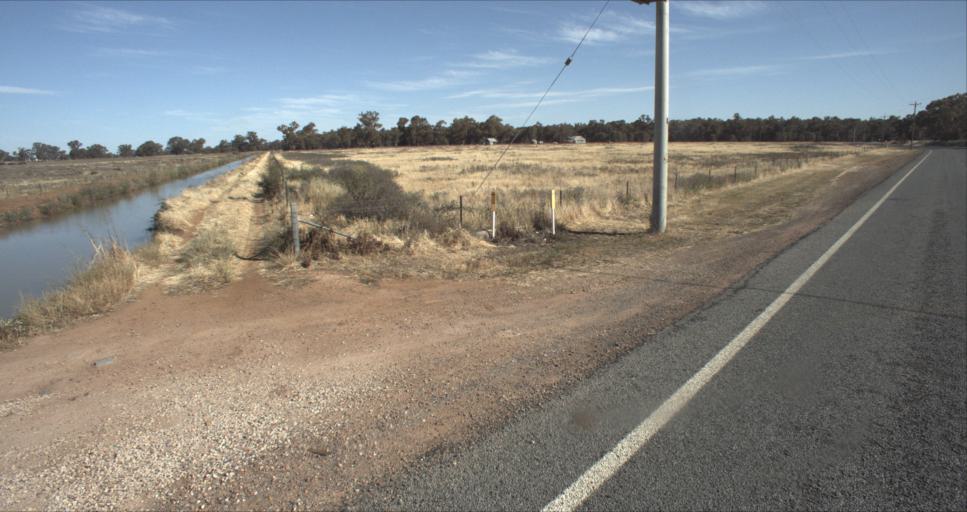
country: AU
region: New South Wales
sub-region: Leeton
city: Leeton
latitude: -34.6213
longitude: 146.3968
